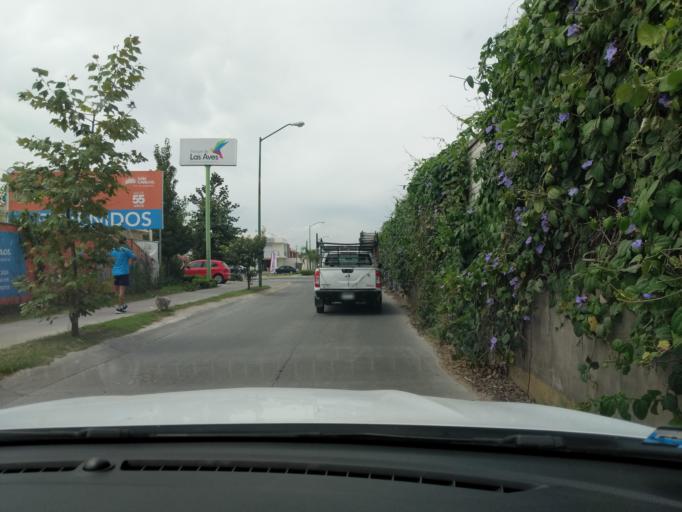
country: MX
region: Jalisco
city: Tesistan
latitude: 20.7905
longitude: -103.4885
